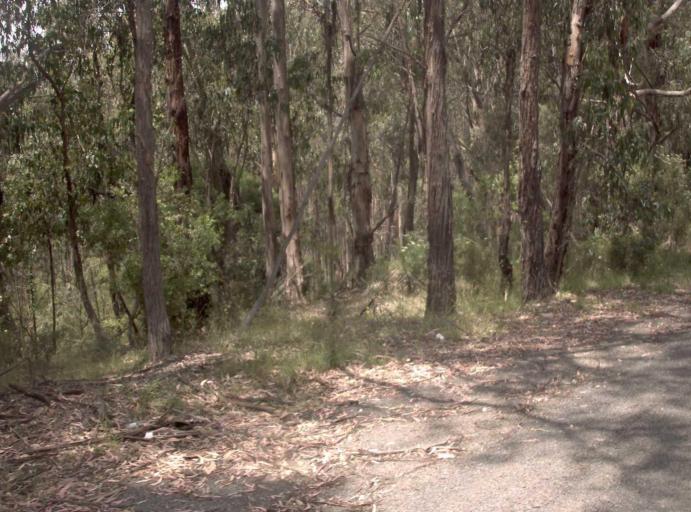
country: AU
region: Victoria
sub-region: Latrobe
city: Traralgon
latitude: -38.3841
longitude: 146.7567
